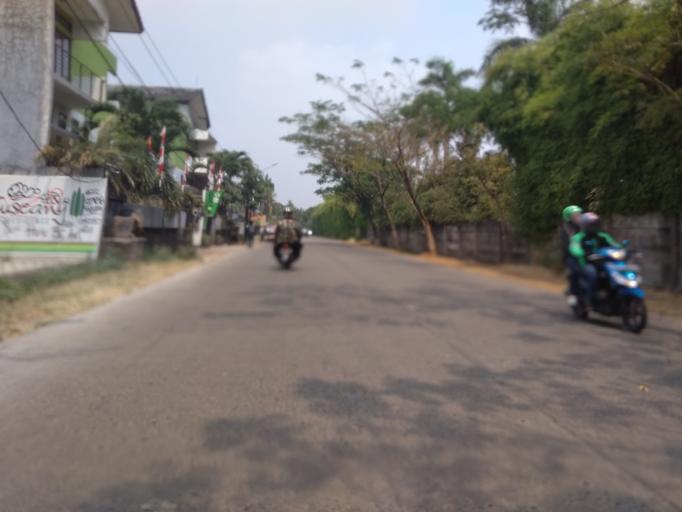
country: ID
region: West Java
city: Pamulang
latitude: -6.3170
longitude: 106.7893
